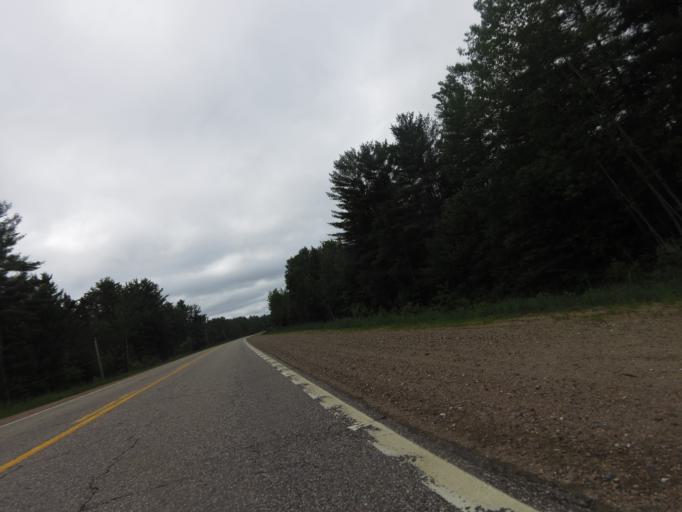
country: CA
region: Quebec
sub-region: Outaouais
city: Shawville
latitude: 45.8648
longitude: -76.4072
